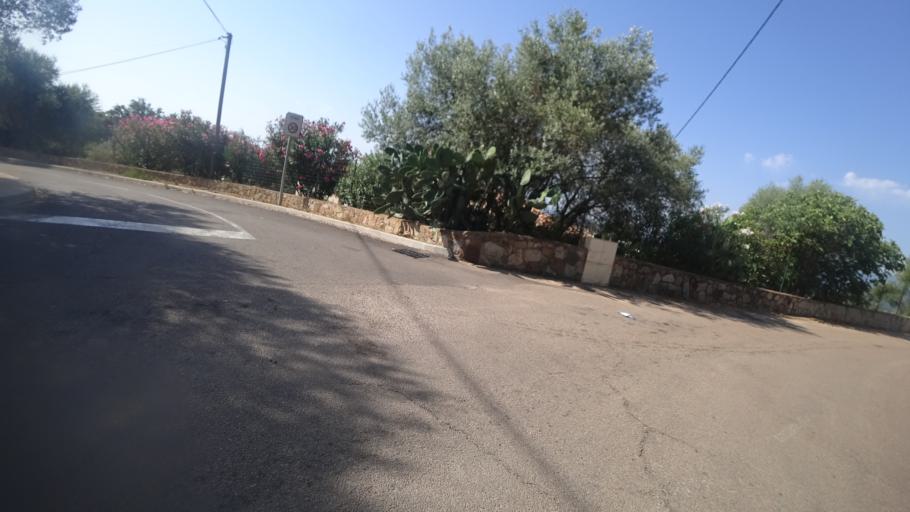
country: FR
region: Corsica
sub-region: Departement de la Corse-du-Sud
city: Porto-Vecchio
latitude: 41.6619
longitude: 9.3276
